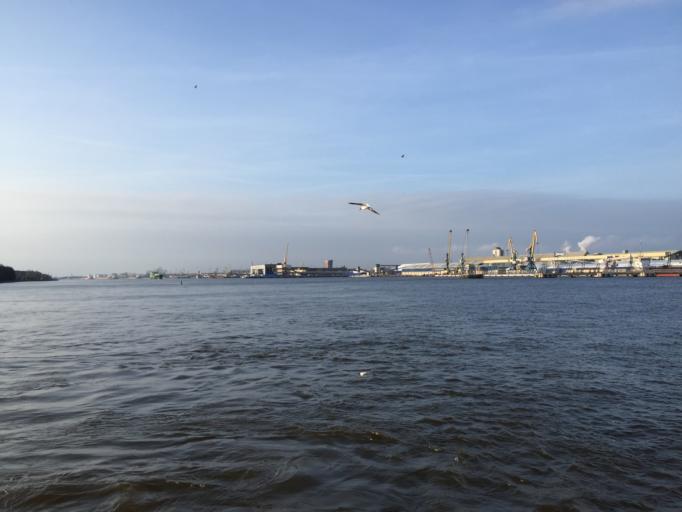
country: LT
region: Klaipedos apskritis
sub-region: Klaipeda
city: Klaipeda
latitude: 55.6862
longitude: 21.1315
